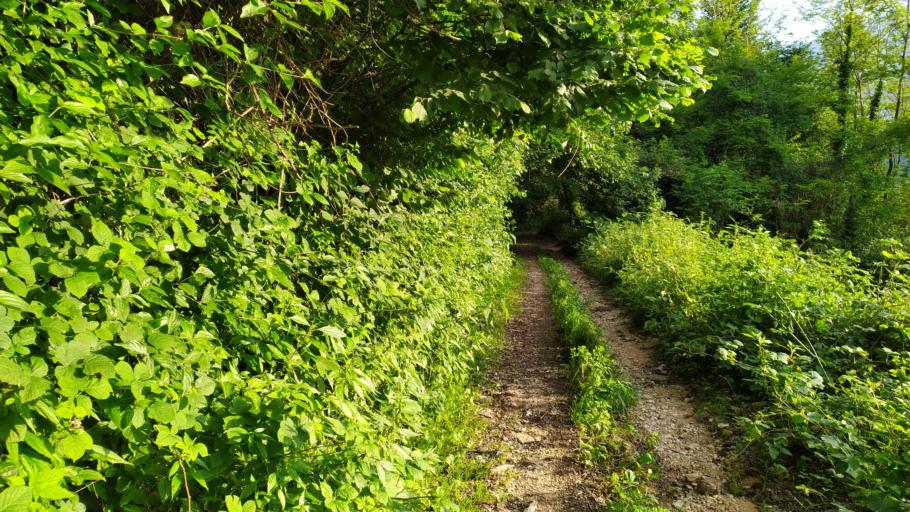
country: IT
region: Veneto
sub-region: Provincia di Vicenza
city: San Quirico
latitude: 45.6864
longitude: 11.2786
